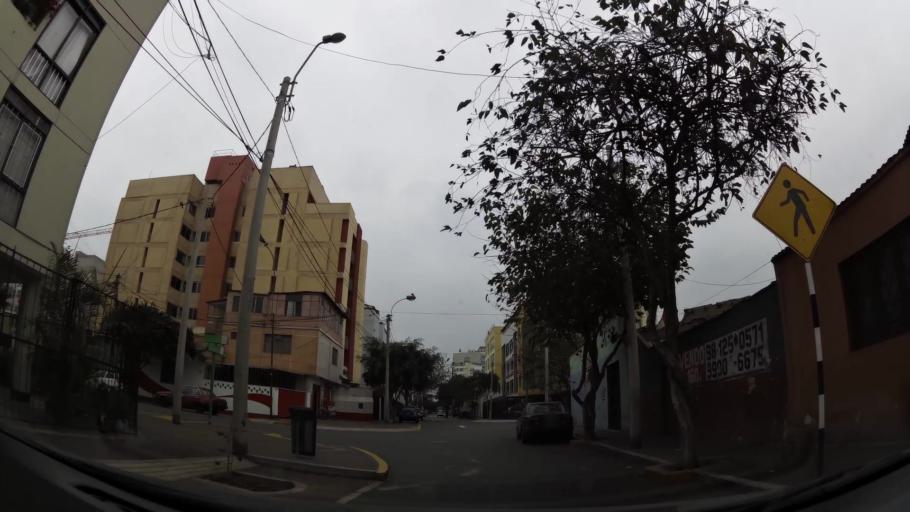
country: PE
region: Lima
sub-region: Lima
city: San Isidro
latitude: -12.1224
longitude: -77.0336
